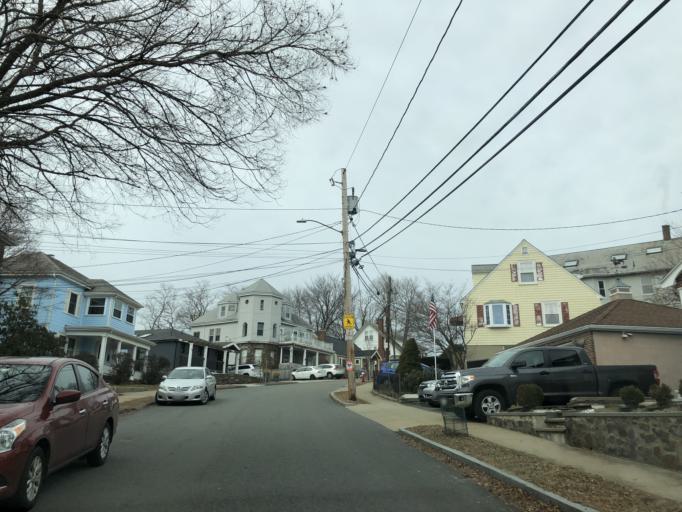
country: US
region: Massachusetts
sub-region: Middlesex County
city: Watertown
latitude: 42.3662
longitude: -71.1690
